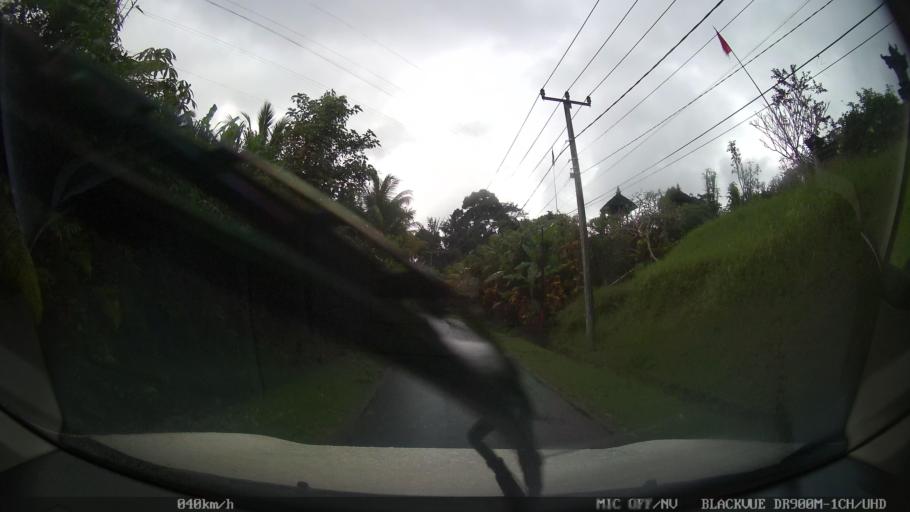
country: ID
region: Bali
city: Banjar Tengah
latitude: -8.4960
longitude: 115.1882
